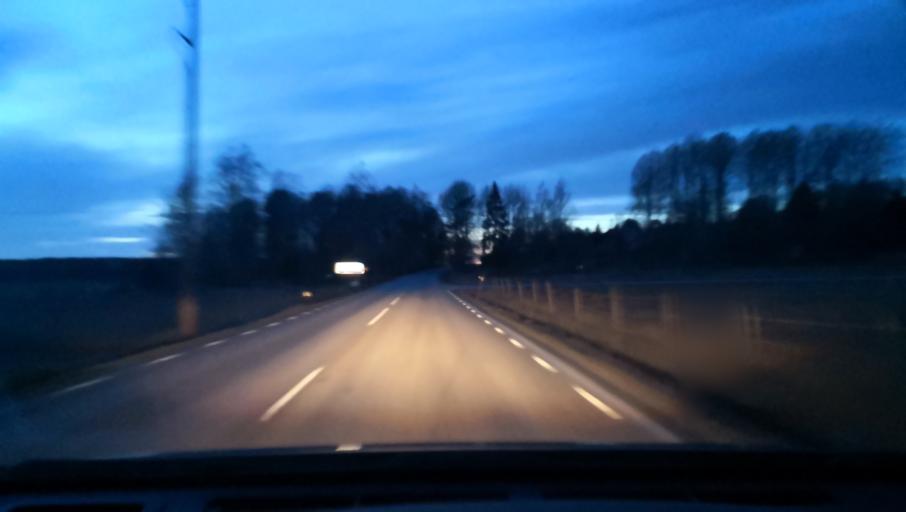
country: SE
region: Uppsala
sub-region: Enkopings Kommun
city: Grillby
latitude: 59.6096
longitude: 17.2741
